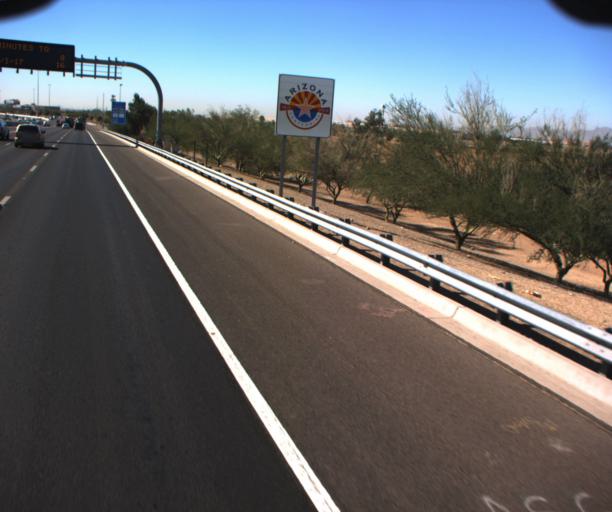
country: US
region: Arizona
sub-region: Maricopa County
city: Peoria
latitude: 33.5511
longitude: -112.2673
